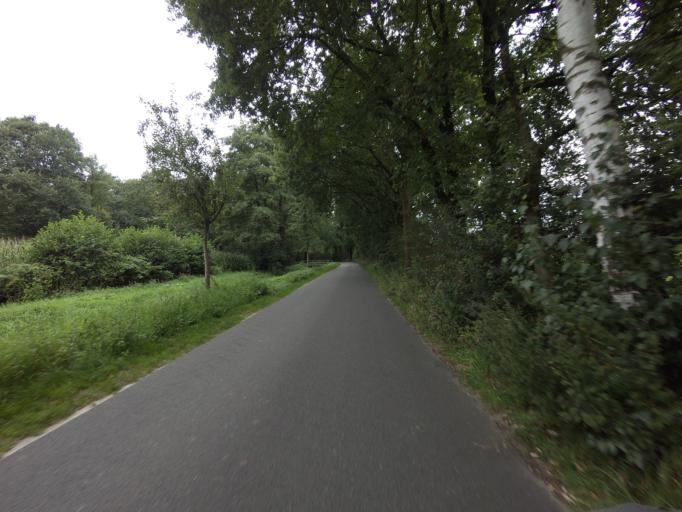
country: DE
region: Lower Saxony
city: Lage
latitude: 52.4661
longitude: 6.9515
